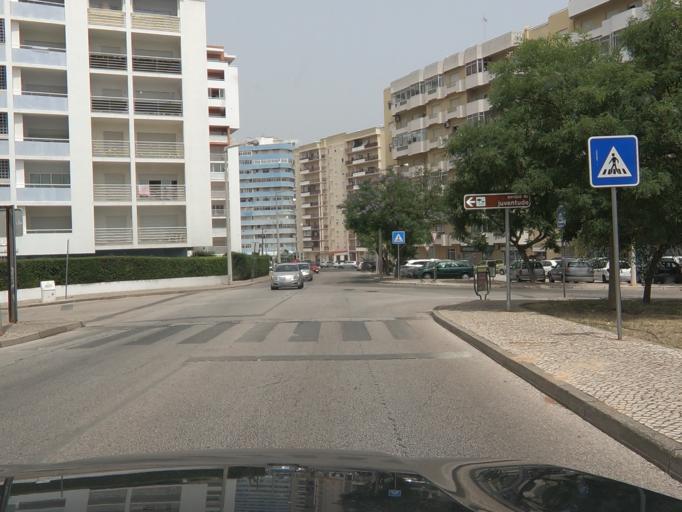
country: PT
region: Faro
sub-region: Portimao
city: Portimao
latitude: 37.1305
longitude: -8.5426
